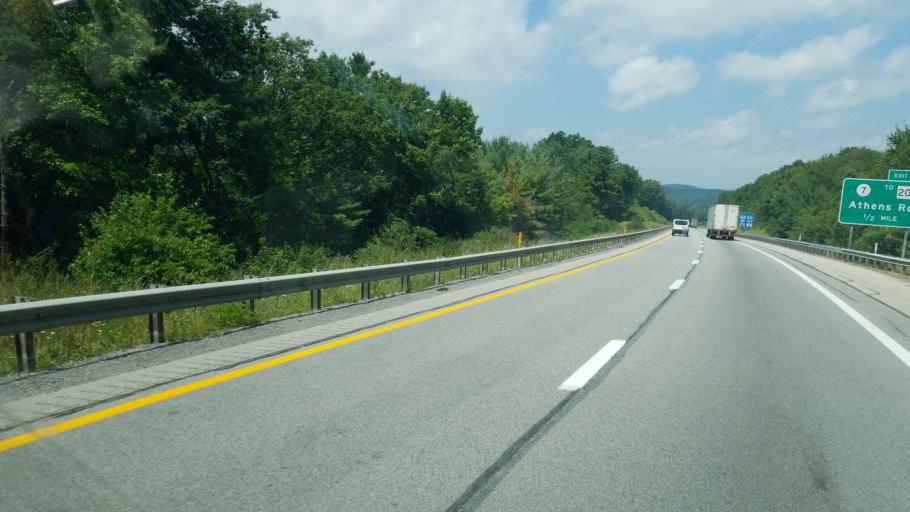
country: US
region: West Virginia
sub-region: Mercer County
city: Athens
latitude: 37.4138
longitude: -81.0621
